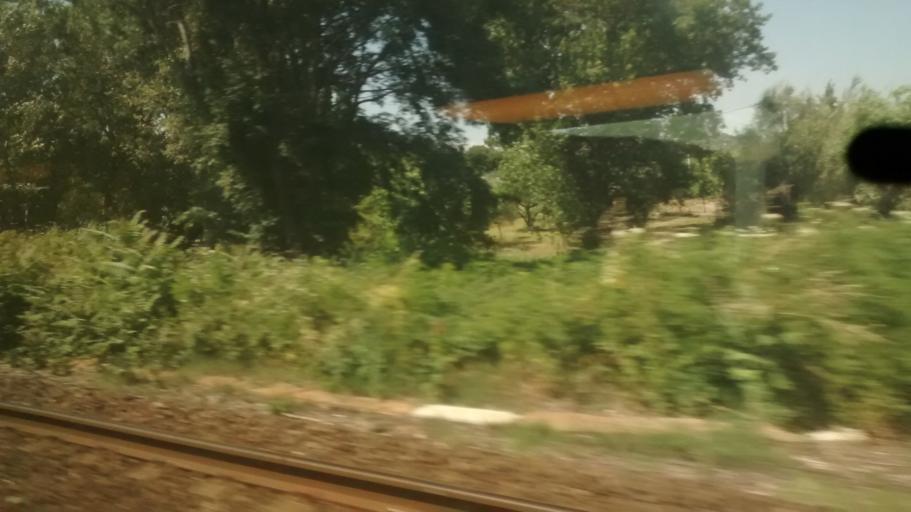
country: FR
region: Languedoc-Roussillon
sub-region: Departement de l'Herault
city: Lunel
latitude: 43.6796
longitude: 4.1200
